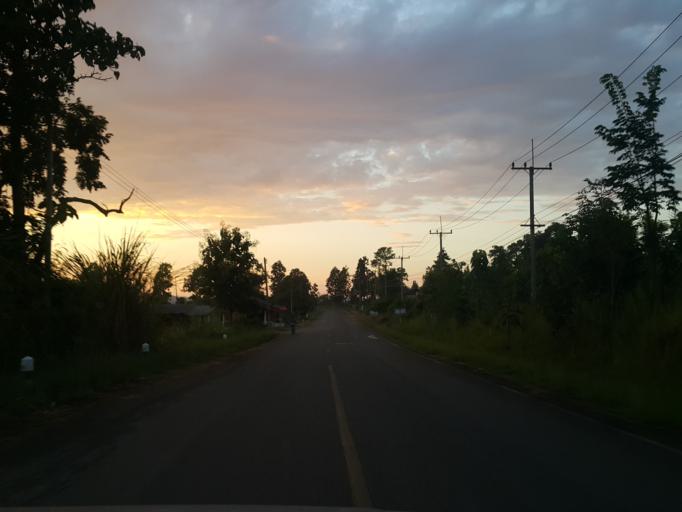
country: TH
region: Mae Hong Son
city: Khun Yuam
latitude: 18.8446
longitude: 97.9627
